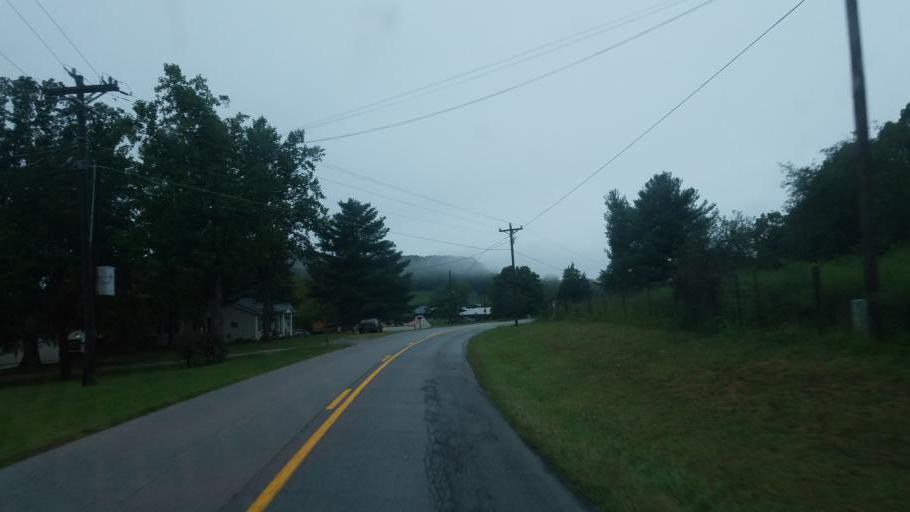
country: US
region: Kentucky
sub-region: Fleming County
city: Flemingsburg
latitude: 38.4045
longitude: -83.6390
